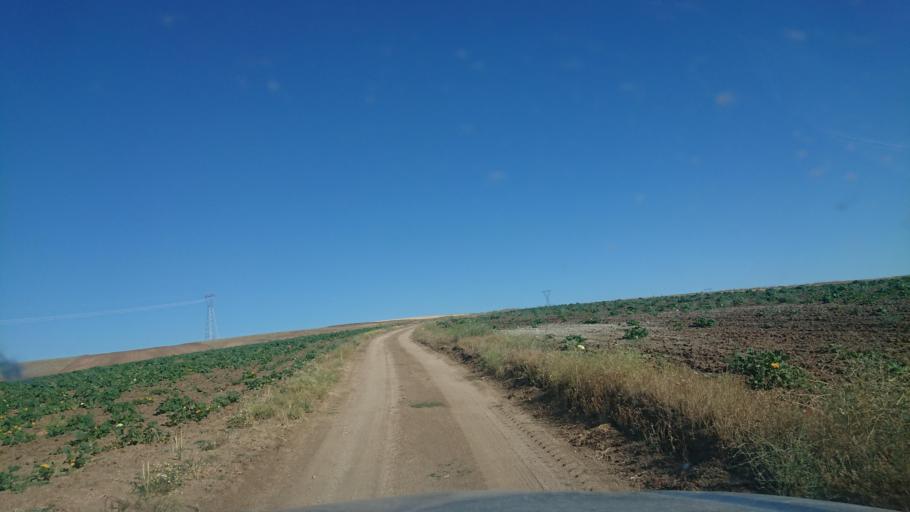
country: TR
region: Aksaray
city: Agacoren
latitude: 38.8326
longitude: 33.9494
